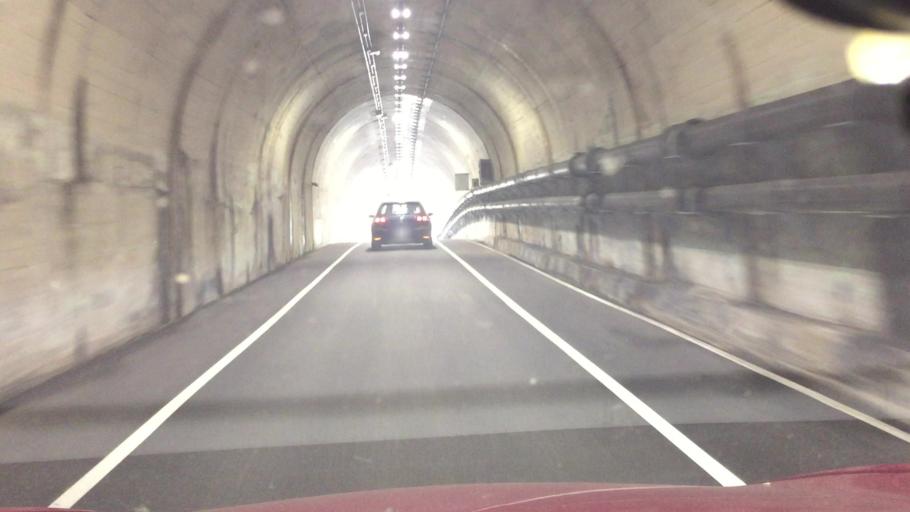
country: US
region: California
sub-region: Marin County
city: Sausalito
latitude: 37.8415
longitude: -122.4923
